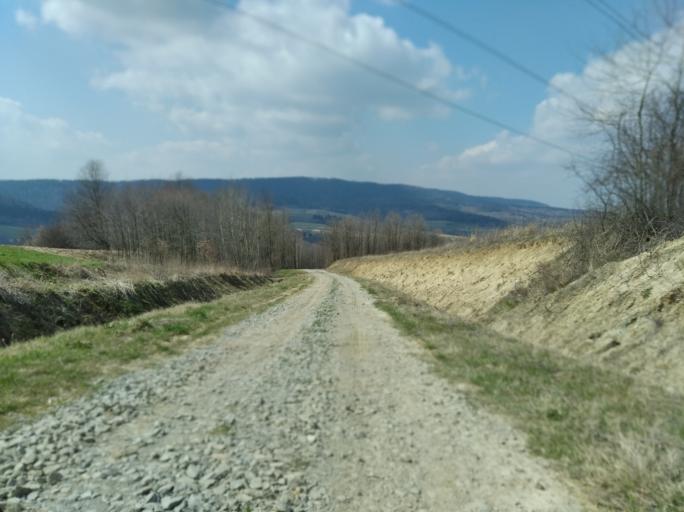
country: PL
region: Subcarpathian Voivodeship
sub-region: Powiat strzyzowski
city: Jawornik
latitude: 49.8212
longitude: 21.8510
